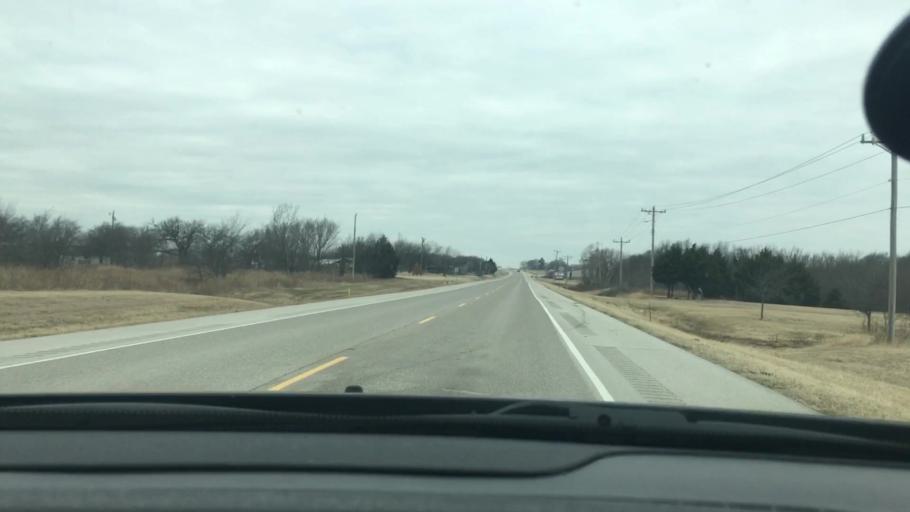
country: US
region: Oklahoma
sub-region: Garvin County
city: Wynnewood
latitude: 34.5104
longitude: -97.3432
